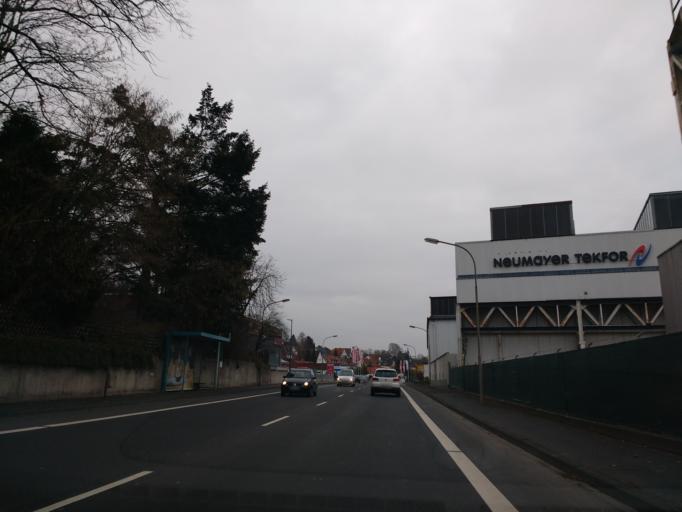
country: DE
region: Hesse
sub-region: Regierungsbezirk Kassel
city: Rotenburg an der Fulda
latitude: 51.0026
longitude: 9.7269
